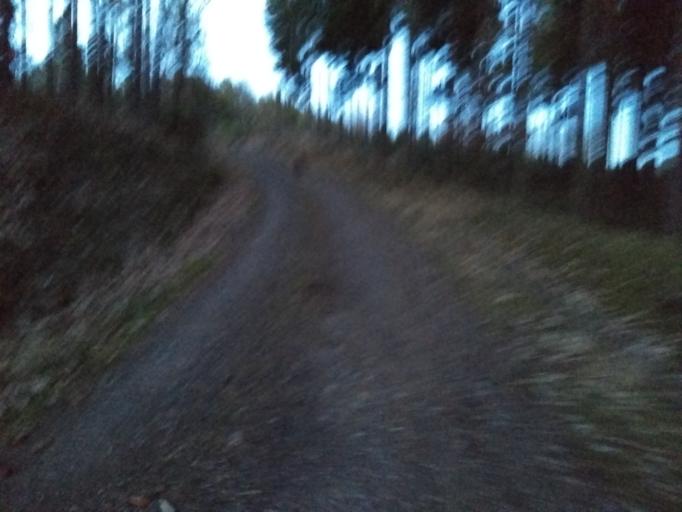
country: CZ
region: Central Bohemia
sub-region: Okres Beroun
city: Lodenice
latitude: 50.0385
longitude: 14.1493
